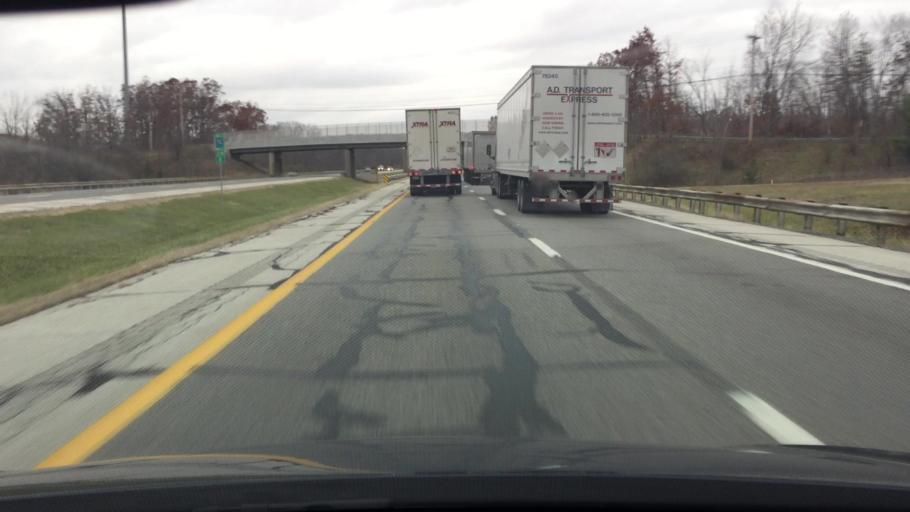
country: US
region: Ohio
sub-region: Mahoning County
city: Canfield
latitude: 41.0556
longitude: -80.7757
